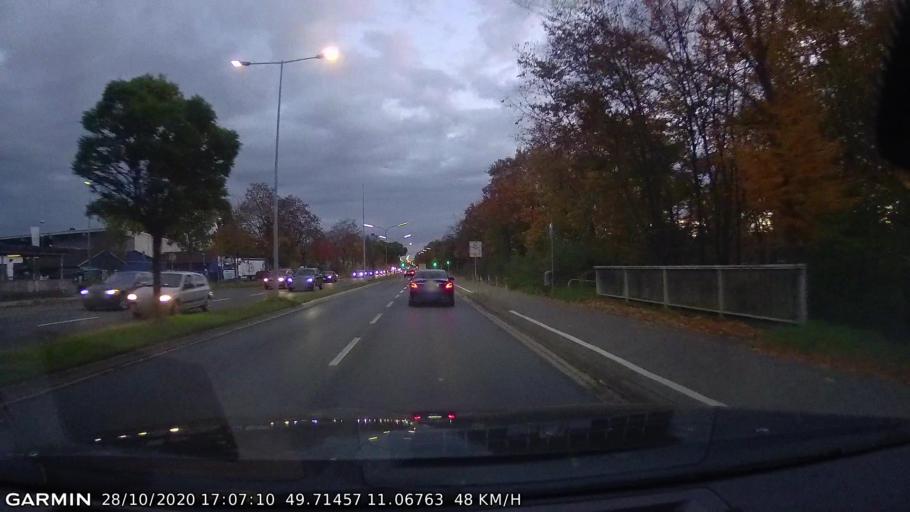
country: DE
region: Bavaria
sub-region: Upper Franconia
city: Forchheim
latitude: 49.7146
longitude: 11.0676
